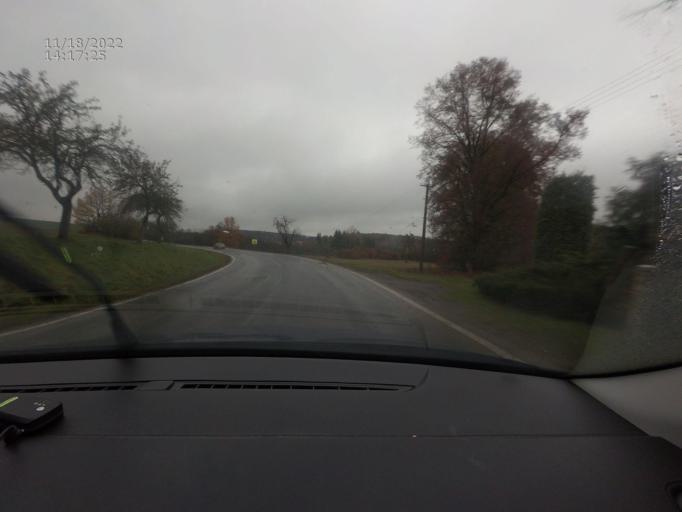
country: CZ
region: Jihocesky
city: Mirotice
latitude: 49.4351
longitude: 14.0479
